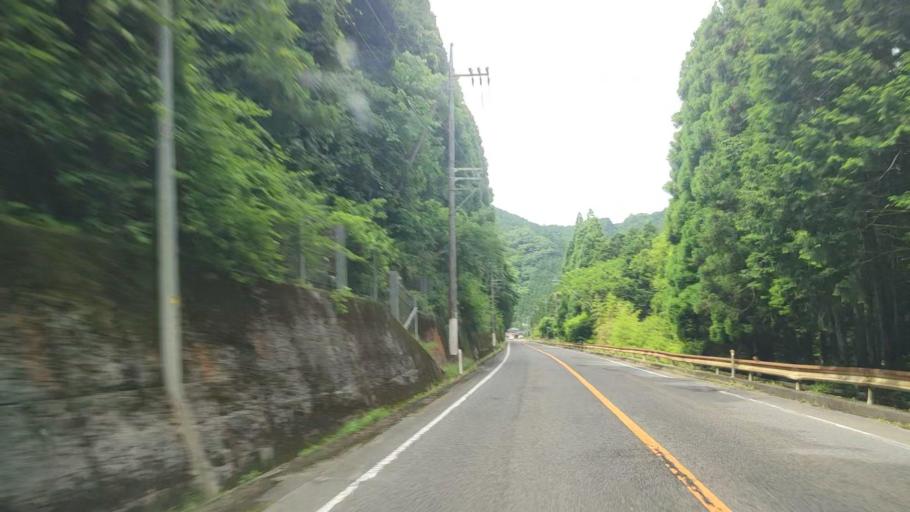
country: JP
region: Okayama
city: Niimi
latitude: 35.0882
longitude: 133.6484
